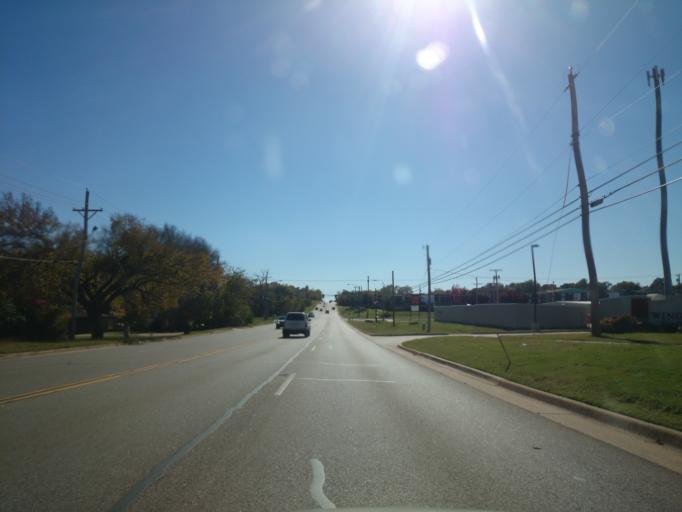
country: US
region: Oklahoma
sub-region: Payne County
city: Stillwater
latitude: 36.1609
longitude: -97.0698
